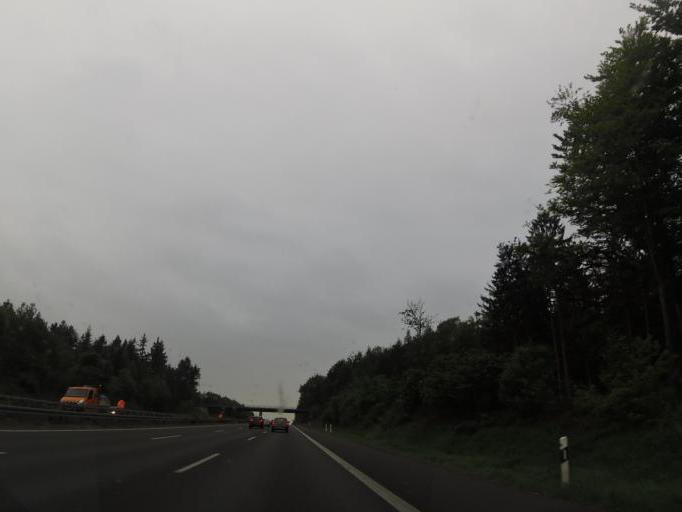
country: DE
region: Lower Saxony
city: Hannoversch Munden
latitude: 51.3859
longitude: 9.6610
